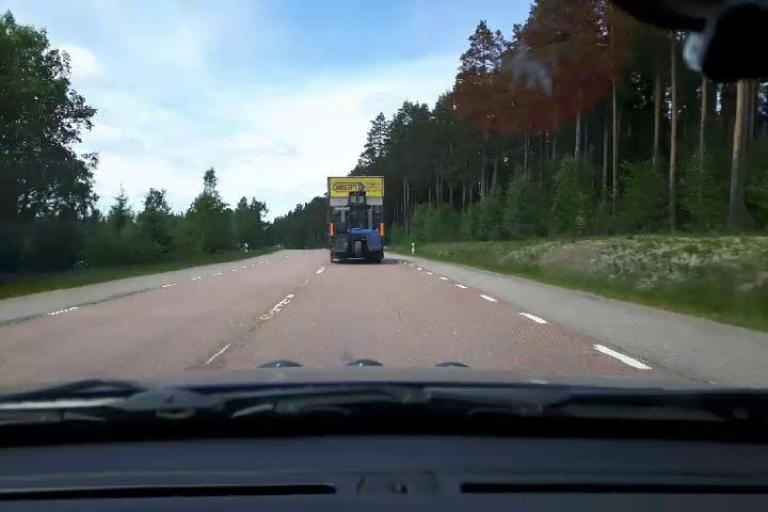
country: SE
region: Uppsala
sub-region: Osthammars Kommun
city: Bjorklinge
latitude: 60.1439
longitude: 17.5021
